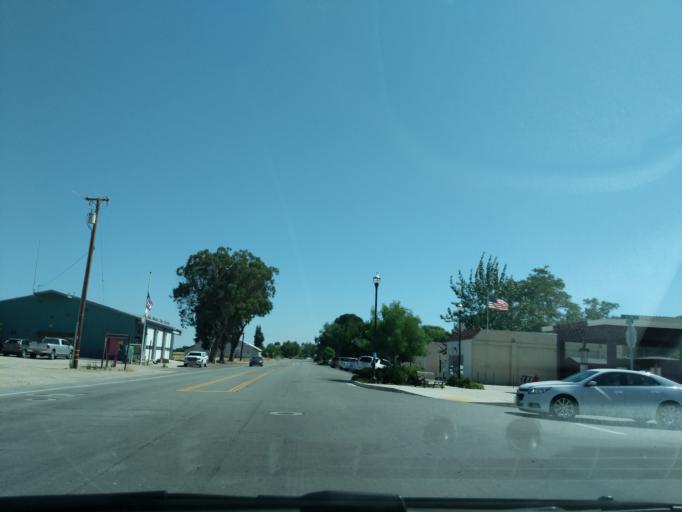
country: US
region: California
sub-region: San Luis Obispo County
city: San Miguel
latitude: 35.7502
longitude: -120.6965
